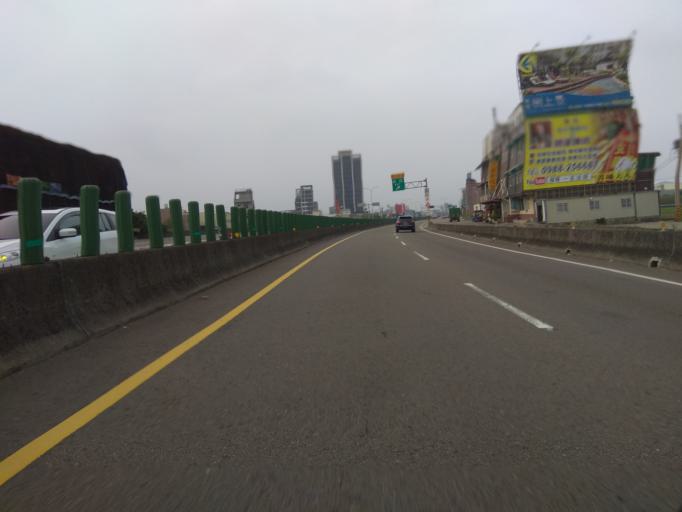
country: TW
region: Taiwan
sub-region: Miaoli
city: Miaoli
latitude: 24.6961
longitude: 120.8635
